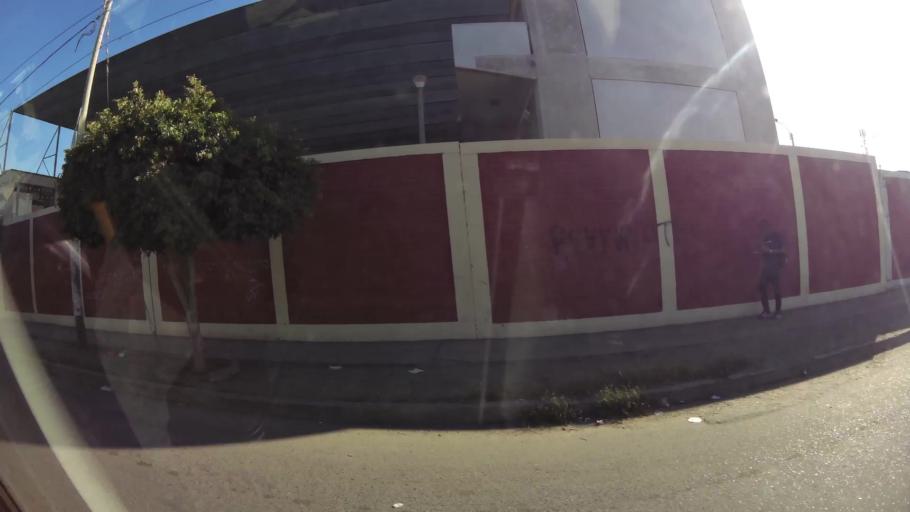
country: PE
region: Ica
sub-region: Provincia de Ica
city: La Tinguina
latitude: -14.0444
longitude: -75.7064
